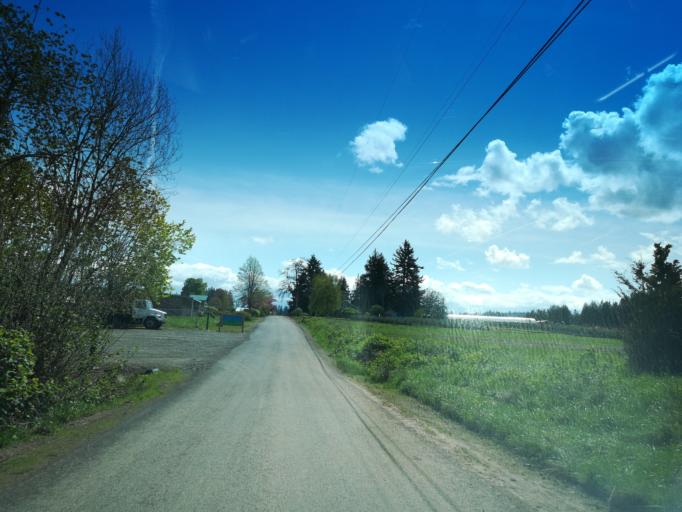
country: US
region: Oregon
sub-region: Clackamas County
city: Damascus
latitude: 45.4440
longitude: -122.4245
